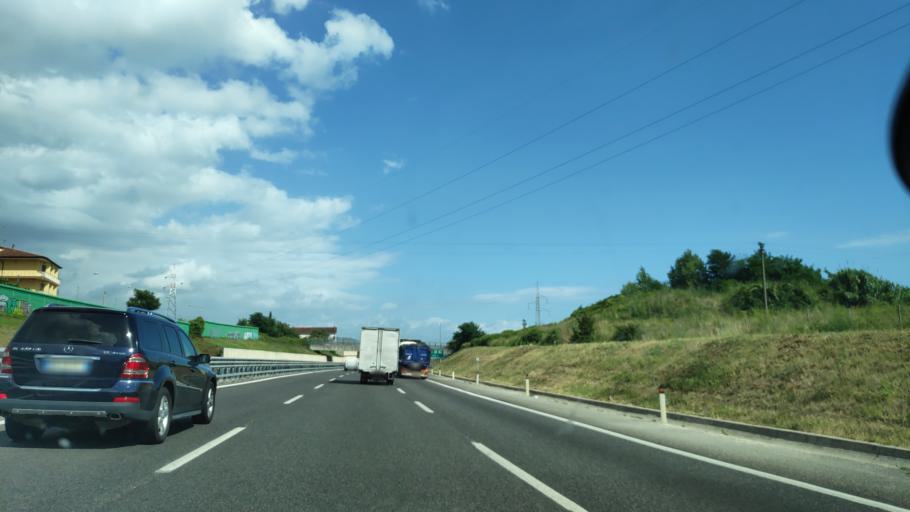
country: IT
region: Campania
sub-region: Provincia di Salerno
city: Piegolelle-San Bartolomeo
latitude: 40.6973
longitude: 14.8265
